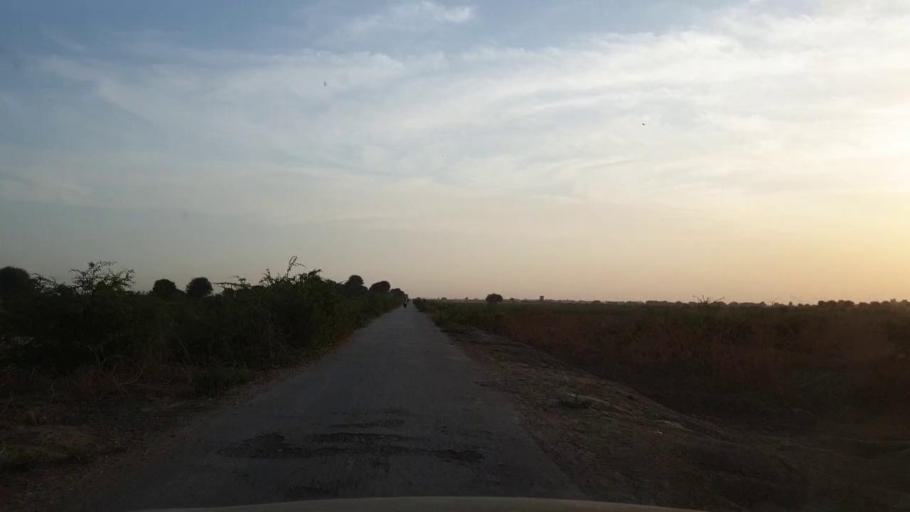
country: PK
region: Sindh
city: Kunri
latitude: 25.1328
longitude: 69.5741
